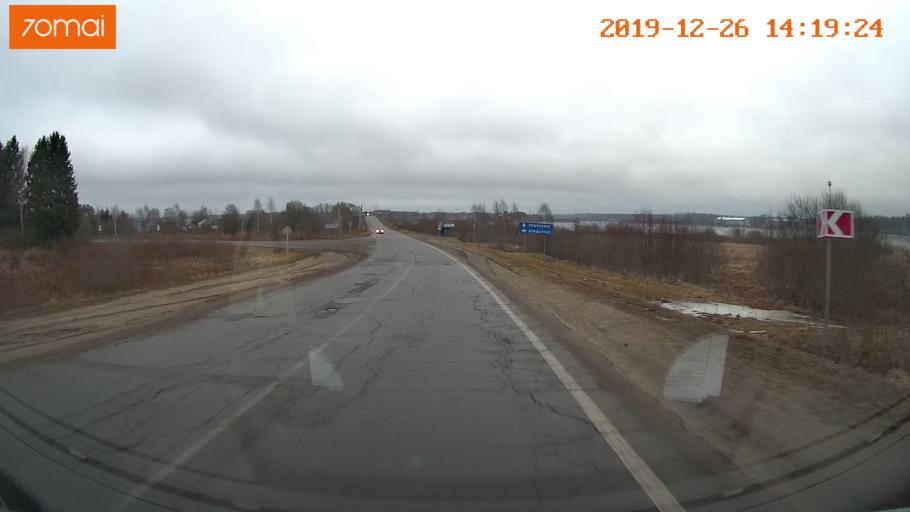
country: RU
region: Jaroslavl
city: Poshekhon'ye
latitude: 58.5106
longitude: 39.1135
